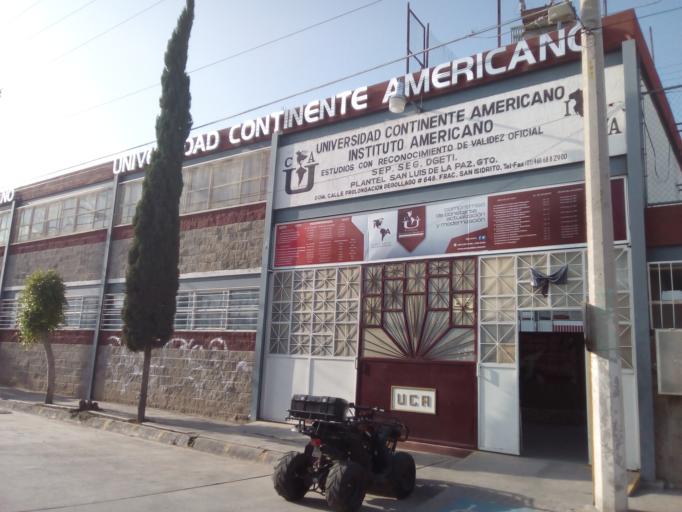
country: MX
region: Guerrero
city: San Luis de la Paz
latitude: 21.2982
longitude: -100.5322
